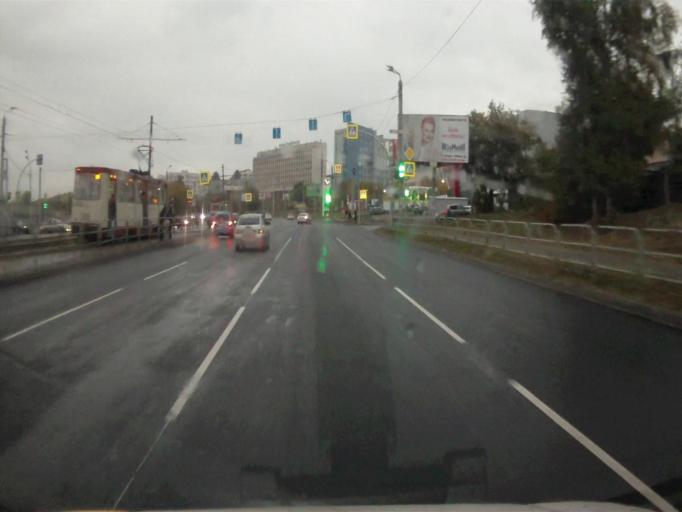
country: RU
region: Chelyabinsk
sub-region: Gorod Chelyabinsk
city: Chelyabinsk
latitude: 55.1877
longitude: 61.3616
